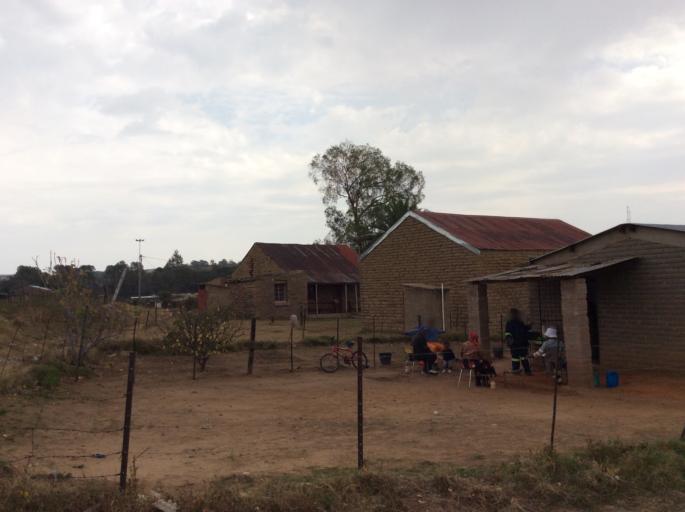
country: ZA
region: Orange Free State
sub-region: Xhariep District Municipality
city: Dewetsdorp
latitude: -29.5861
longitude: 26.6703
